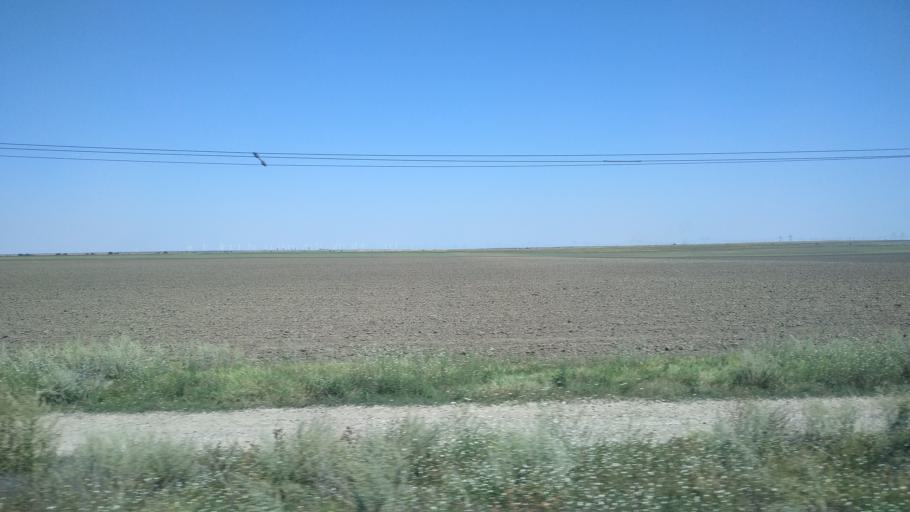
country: RO
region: Ialomita
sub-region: Municipiul Fetesti
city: Fetesti-Gara
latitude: 44.4180
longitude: 27.7869
